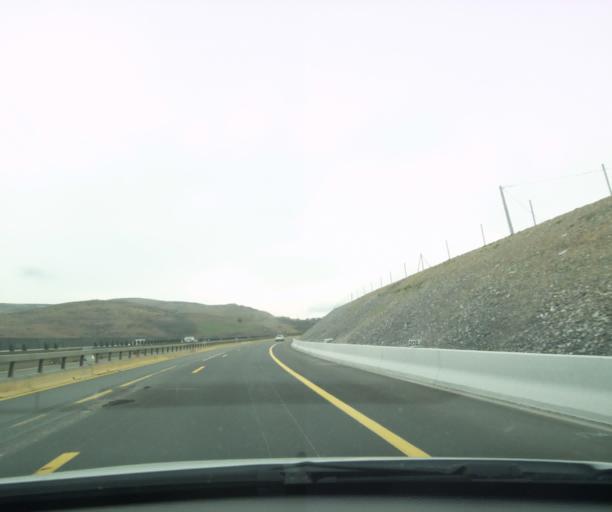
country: FR
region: Aquitaine
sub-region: Departement des Pyrenees-Atlantiques
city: Urrugne
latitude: 43.3500
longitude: -1.7181
